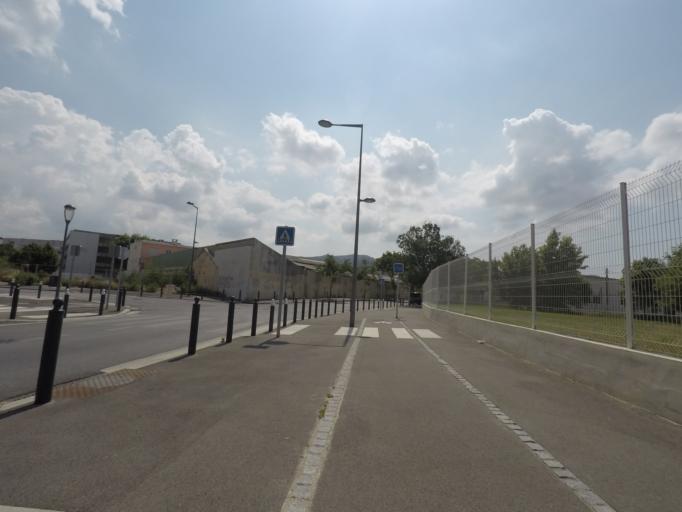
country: FR
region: Provence-Alpes-Cote d'Azur
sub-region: Departement des Bouches-du-Rhone
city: Marseille 10
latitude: 43.2775
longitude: 5.4064
